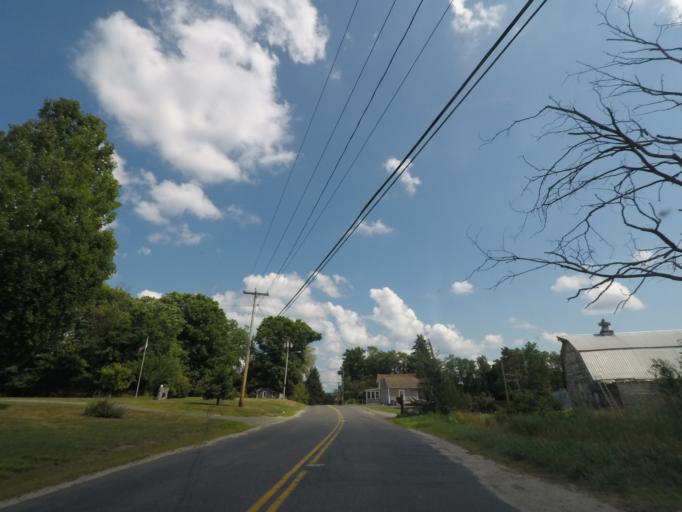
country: US
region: Massachusetts
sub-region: Hampden County
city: Monson
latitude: 42.1162
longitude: -72.3300
